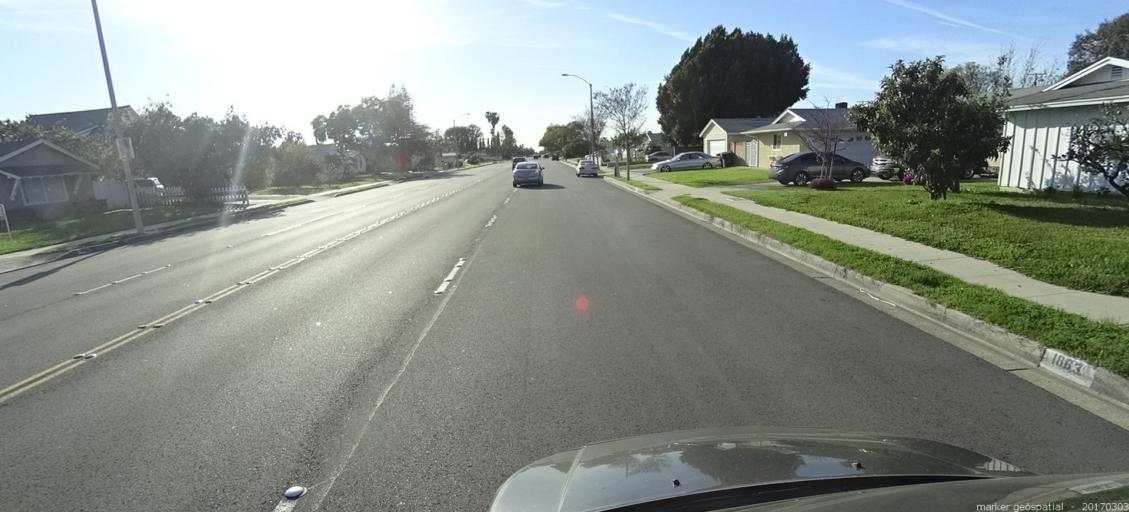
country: US
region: California
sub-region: Orange County
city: Anaheim
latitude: 33.8289
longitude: -117.9489
